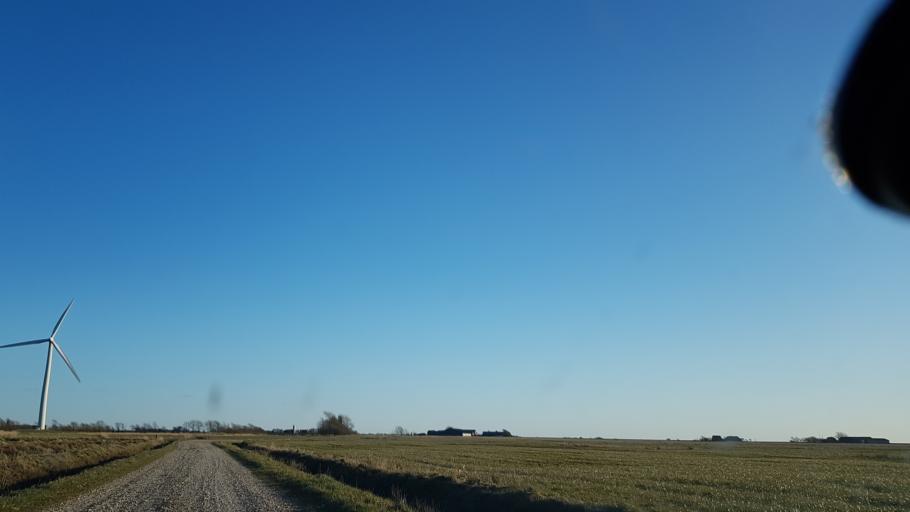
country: DK
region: South Denmark
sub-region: Esbjerg Kommune
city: Bramming
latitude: 55.4098
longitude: 8.6748
